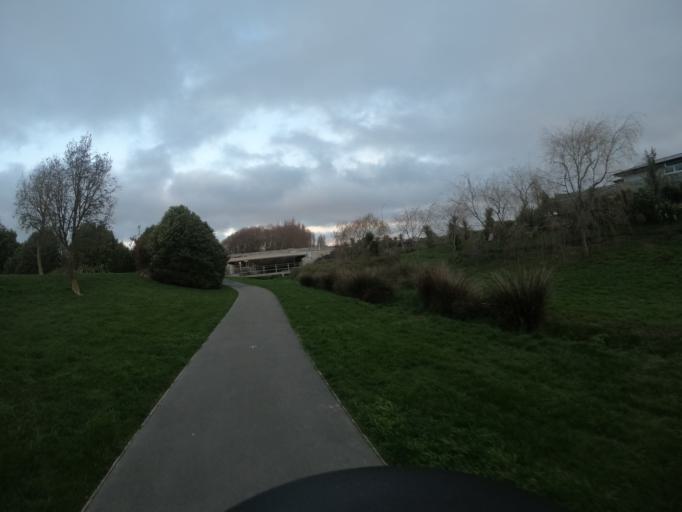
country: NZ
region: Canterbury
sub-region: Selwyn District
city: Prebbleton
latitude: -43.5607
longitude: 172.5606
